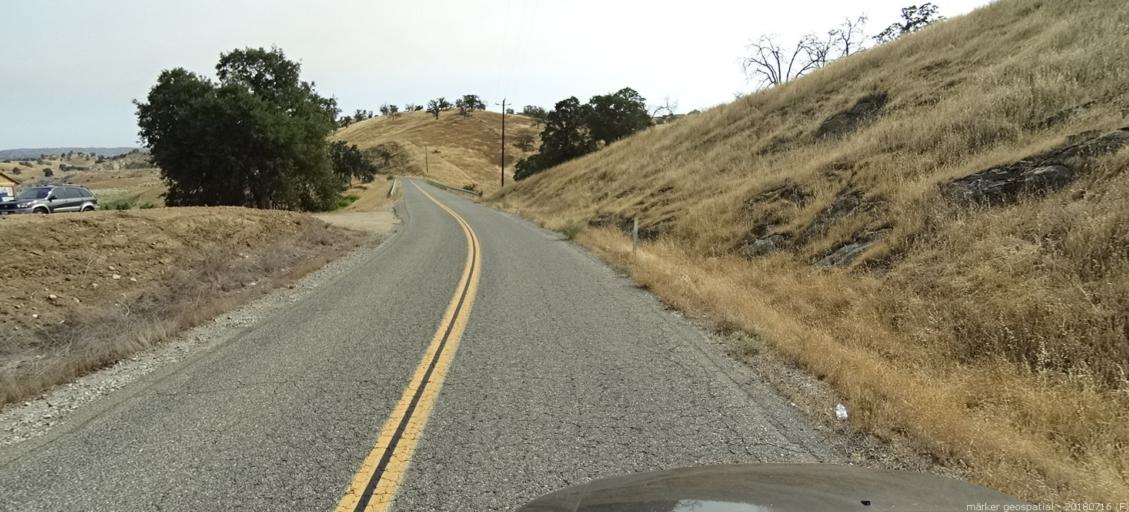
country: US
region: California
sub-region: Madera County
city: Bonadelle Ranchos-Madera Ranchos
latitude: 37.1026
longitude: -119.8696
